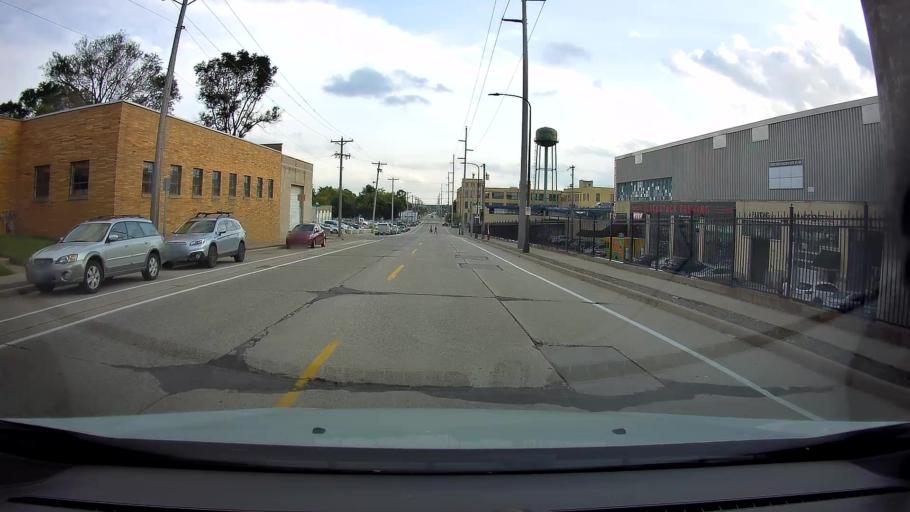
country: US
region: Minnesota
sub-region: Ramsey County
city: Falcon Heights
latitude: 44.9659
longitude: -93.1823
